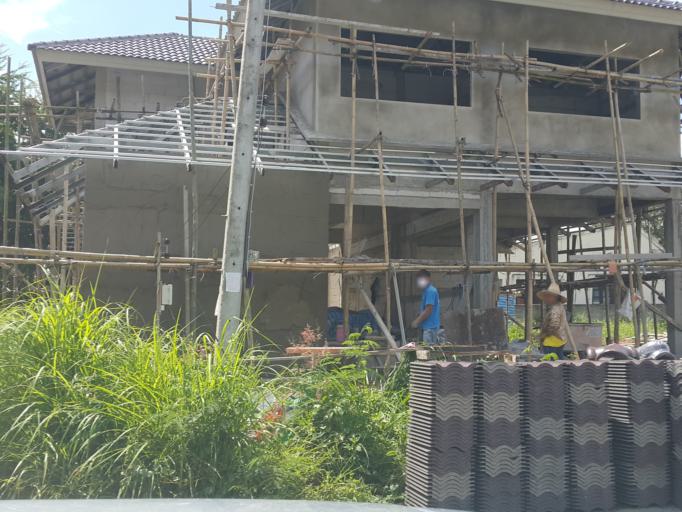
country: TH
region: Chiang Mai
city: Chiang Mai
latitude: 18.7358
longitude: 98.9618
